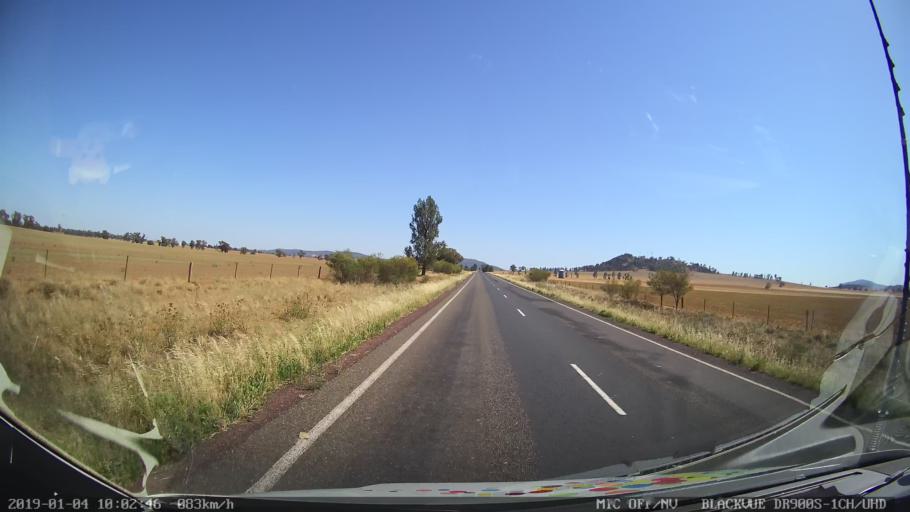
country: AU
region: New South Wales
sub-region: Cabonne
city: Canowindra
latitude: -33.4723
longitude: 148.3651
